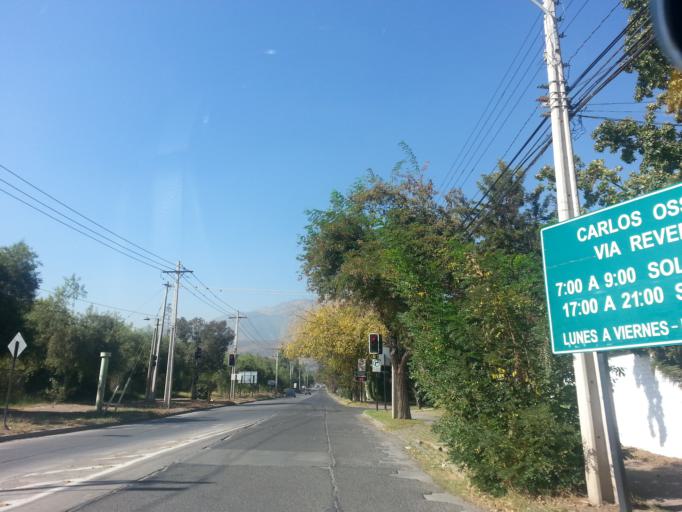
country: CL
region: Santiago Metropolitan
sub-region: Provincia de Santiago
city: Villa Presidente Frei, Nunoa, Santiago, Chile
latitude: -33.4341
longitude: -70.5434
